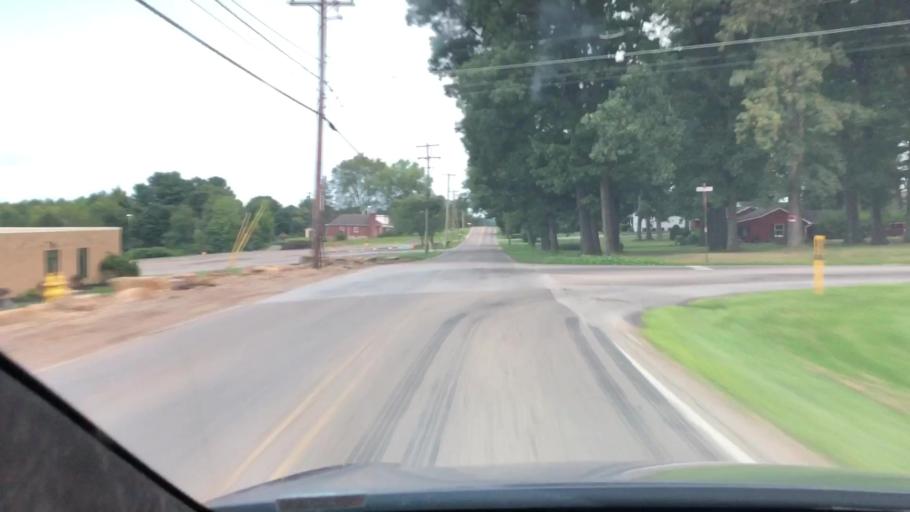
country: US
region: Pennsylvania
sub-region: Butler County
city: Shanor-Northvue
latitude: 40.8934
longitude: -79.9272
